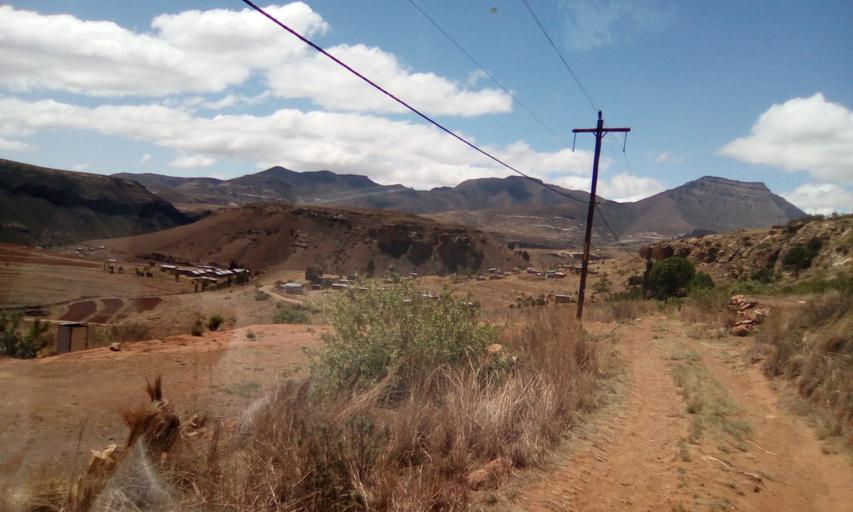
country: LS
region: Qacha's Nek
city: Qacha's Nek
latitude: -30.0686
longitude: 28.6348
